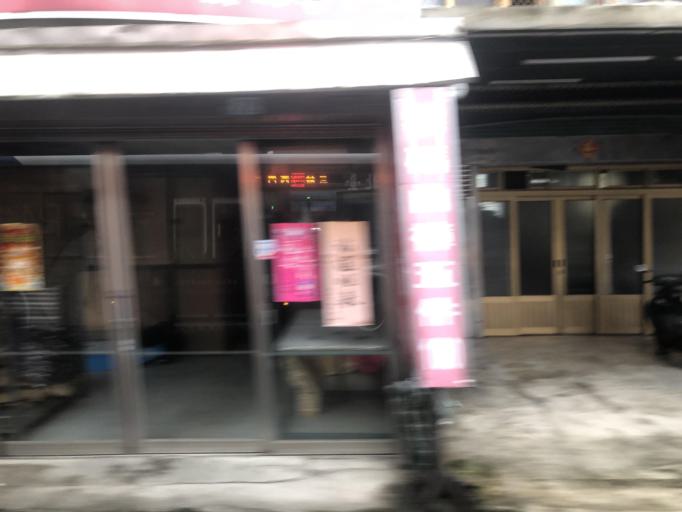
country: TW
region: Taiwan
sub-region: Taoyuan
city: Taoyuan
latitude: 24.9352
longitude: 121.3920
